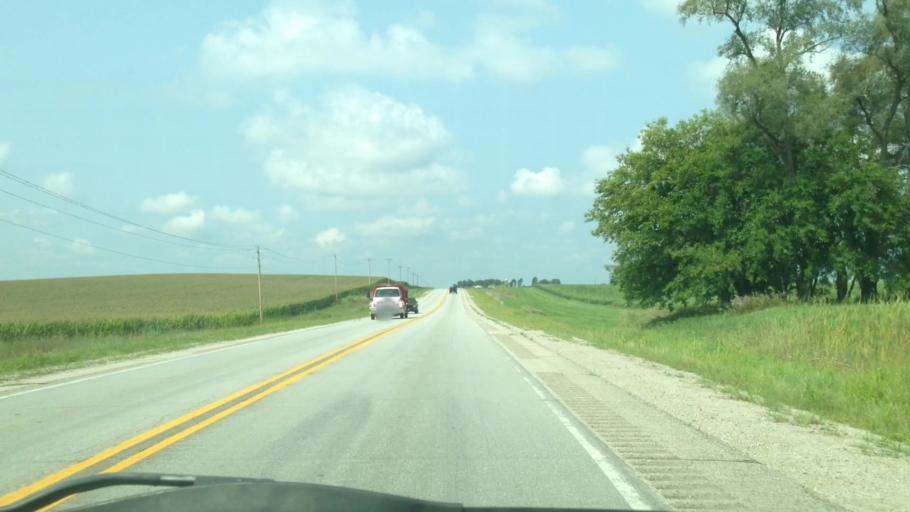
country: US
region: Iowa
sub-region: Benton County
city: Walford
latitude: 41.8762
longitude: -91.8520
